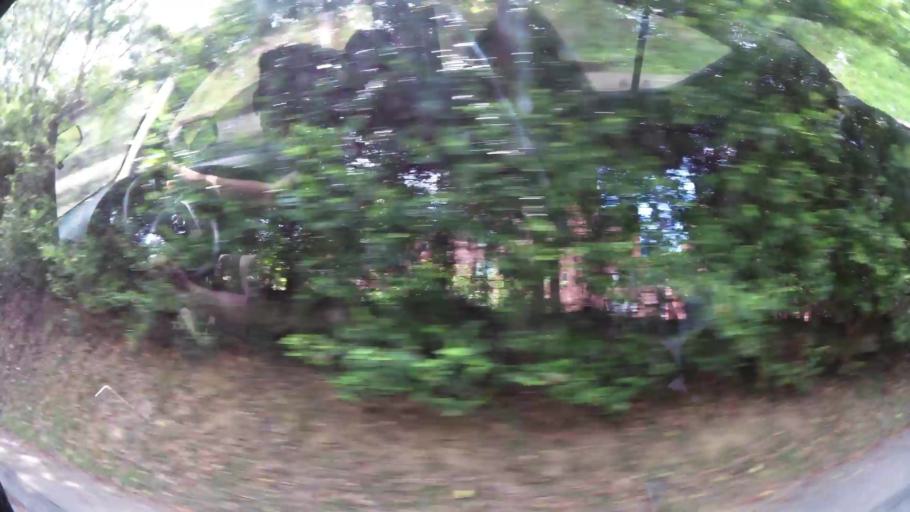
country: CO
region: Antioquia
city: Envigado
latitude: 6.1771
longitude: -75.5881
